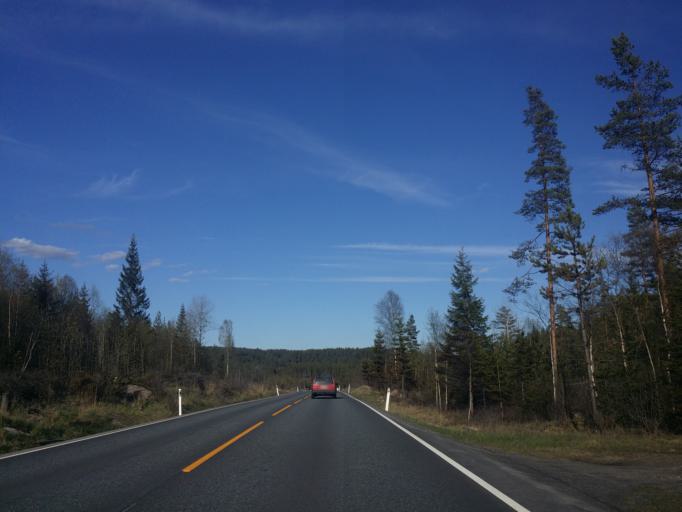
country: NO
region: Buskerud
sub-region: Kongsberg
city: Kongsberg
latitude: 59.6303
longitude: 9.5074
